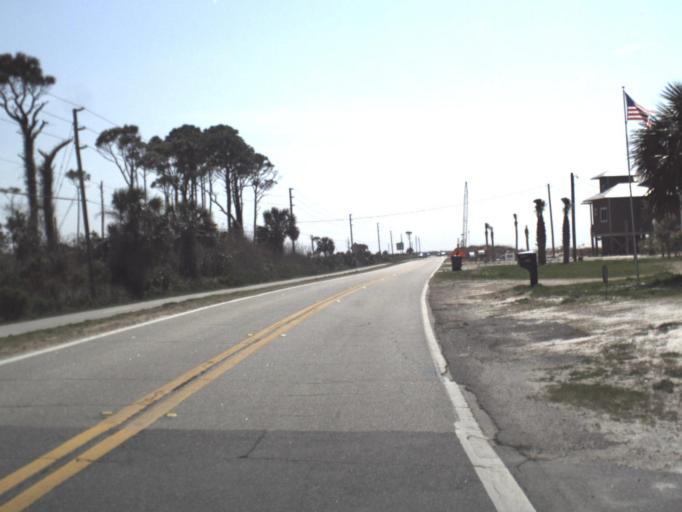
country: US
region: Florida
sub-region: Gulf County
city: Port Saint Joe
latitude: 29.6836
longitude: -85.3672
